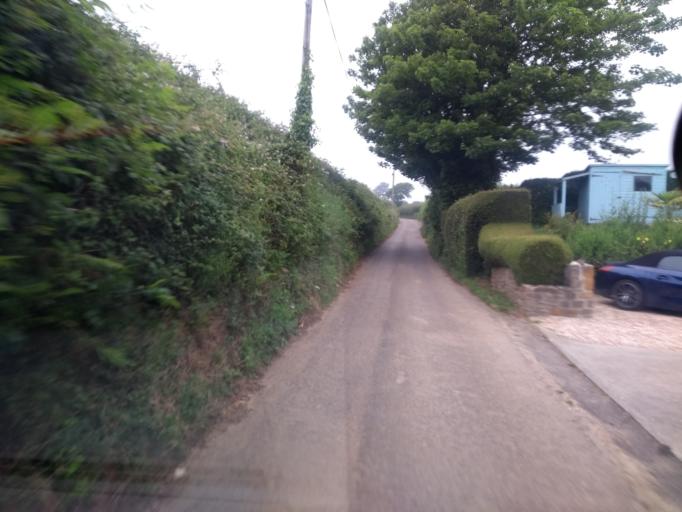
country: GB
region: England
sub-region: Dorset
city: Bridport
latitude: 50.7267
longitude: -2.7792
